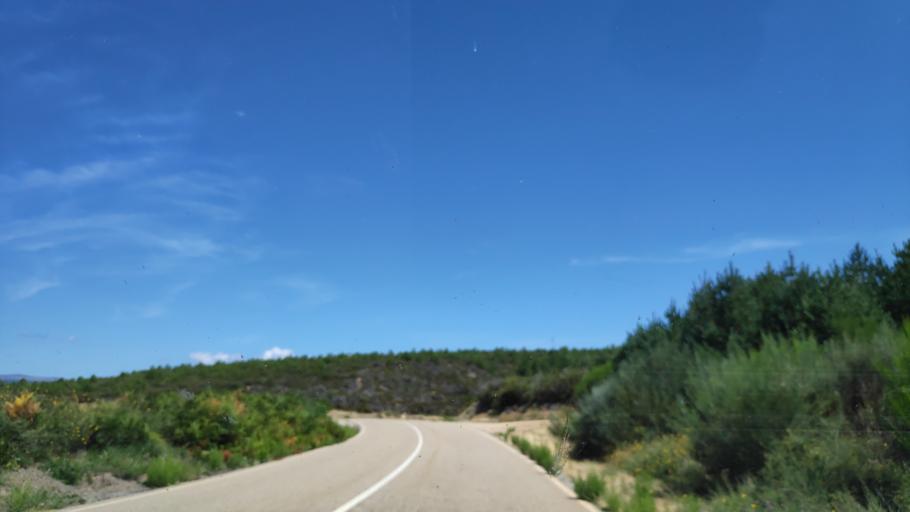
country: ES
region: Castille and Leon
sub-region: Provincia de Zamora
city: Requejo
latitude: 42.0134
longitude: -6.6923
